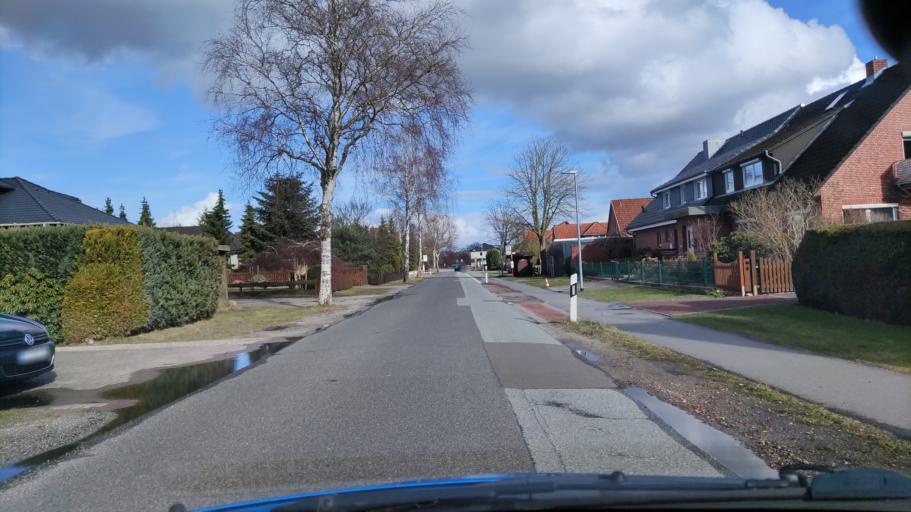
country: DE
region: Lower Saxony
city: Winsen
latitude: 53.3565
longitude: 10.1820
